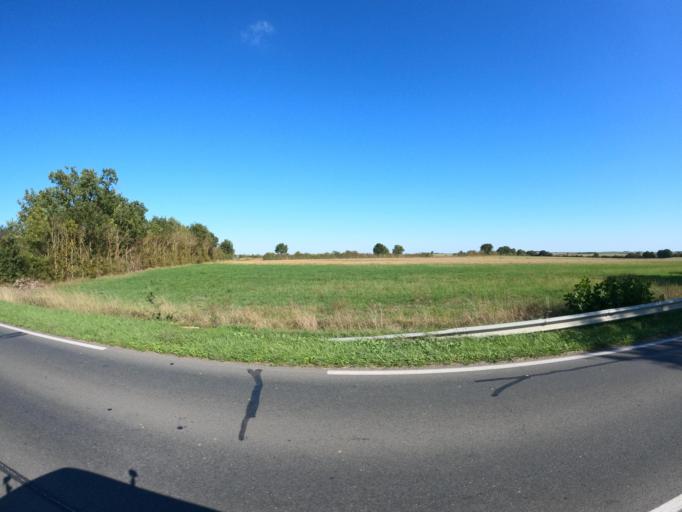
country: FR
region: Poitou-Charentes
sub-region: Departement de la Vienne
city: Ayron
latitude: 46.6607
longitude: 0.0350
